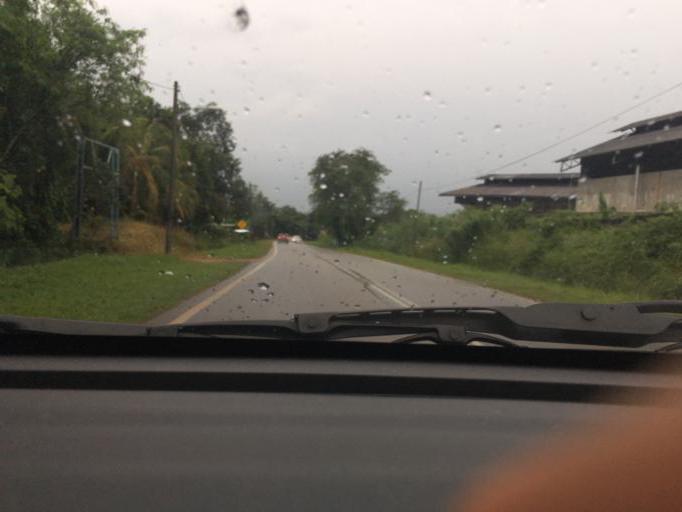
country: MY
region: Kedah
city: Bedong
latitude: 5.6984
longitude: 100.6330
